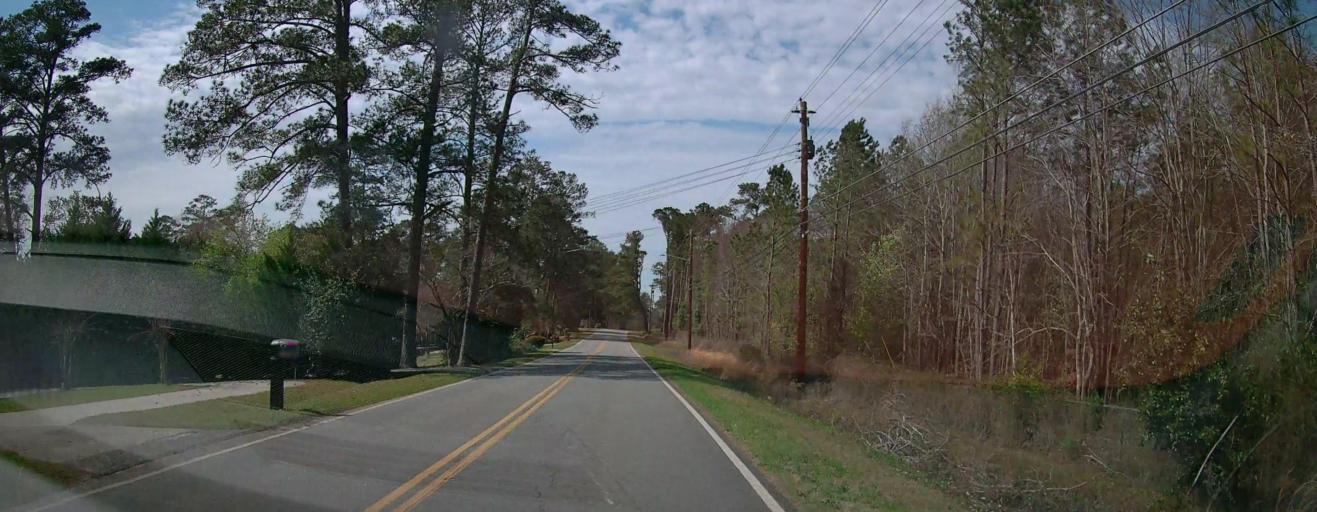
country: US
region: Georgia
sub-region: Bibb County
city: Macon
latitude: 32.8697
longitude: -83.6225
